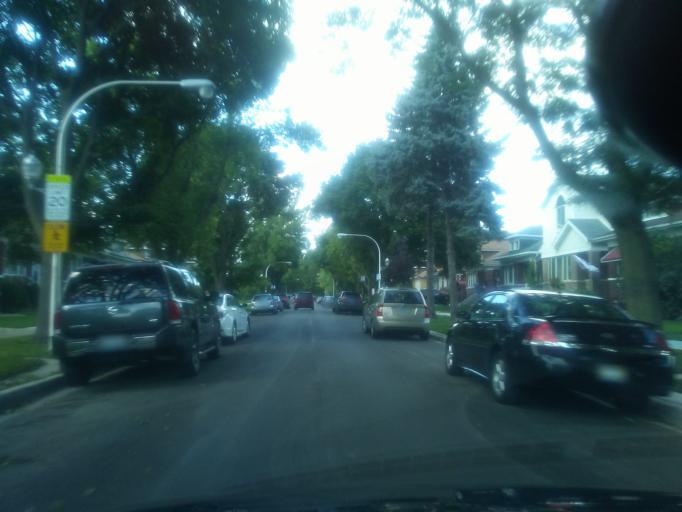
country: US
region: Illinois
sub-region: Cook County
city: Lincolnwood
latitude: 41.9704
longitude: -87.7330
